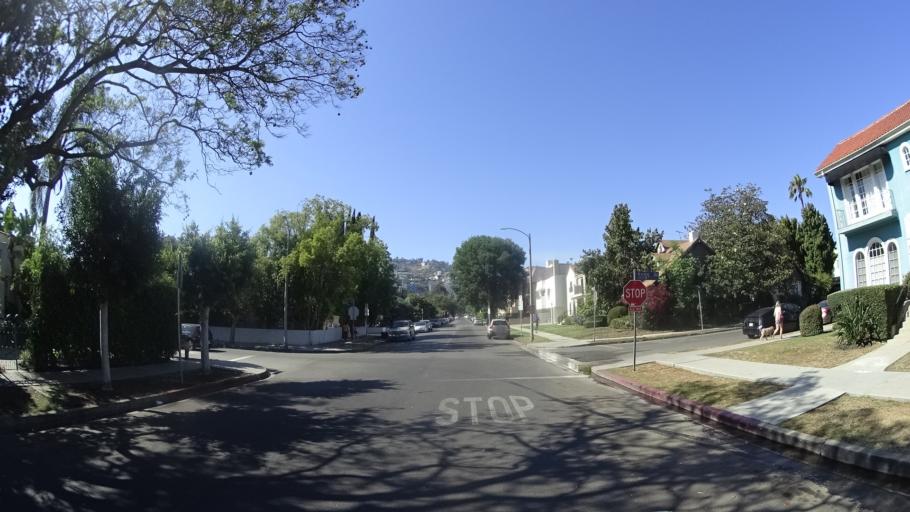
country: US
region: California
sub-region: Los Angeles County
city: West Hollywood
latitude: 34.0851
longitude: -118.3752
